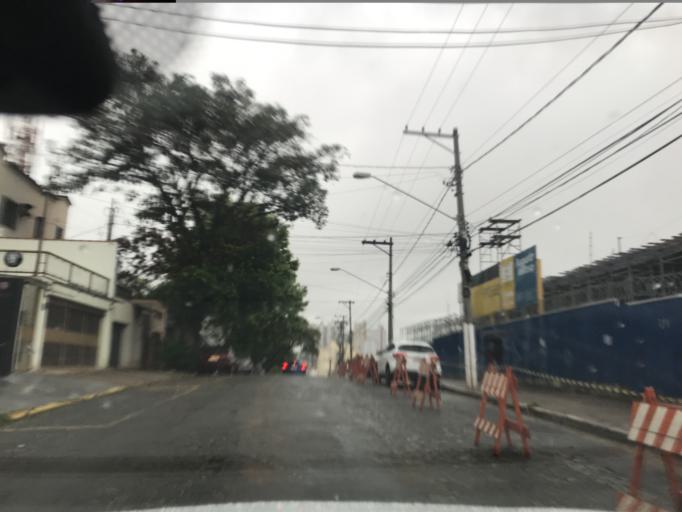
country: BR
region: Sao Paulo
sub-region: Sao Paulo
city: Sao Paulo
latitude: -23.5360
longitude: -46.6877
